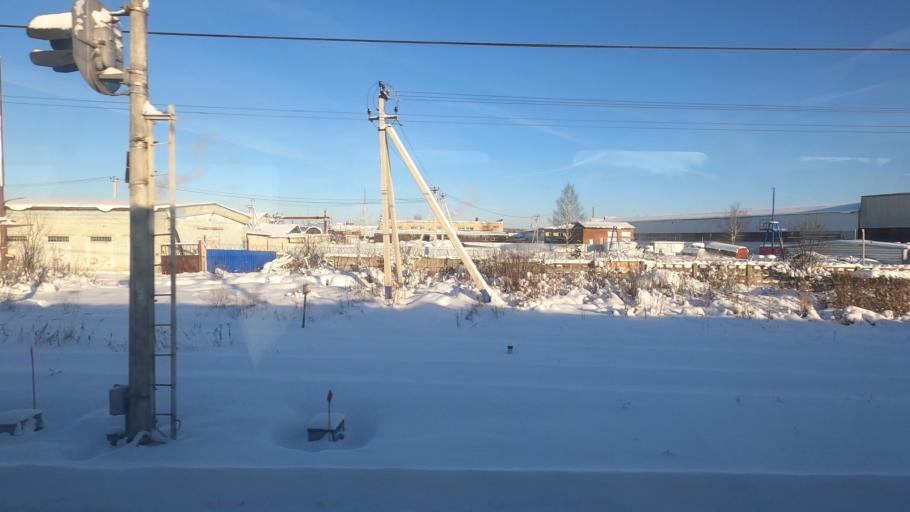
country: RU
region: Moskovskaya
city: Taldom
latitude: 56.7177
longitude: 37.5351
